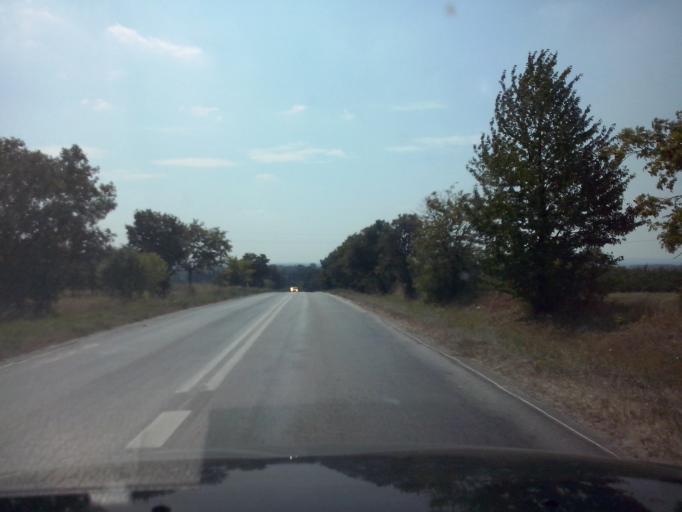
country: PL
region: Swietokrzyskie
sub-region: Powiat staszowski
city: Szydlow
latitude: 50.6030
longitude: 21.0090
